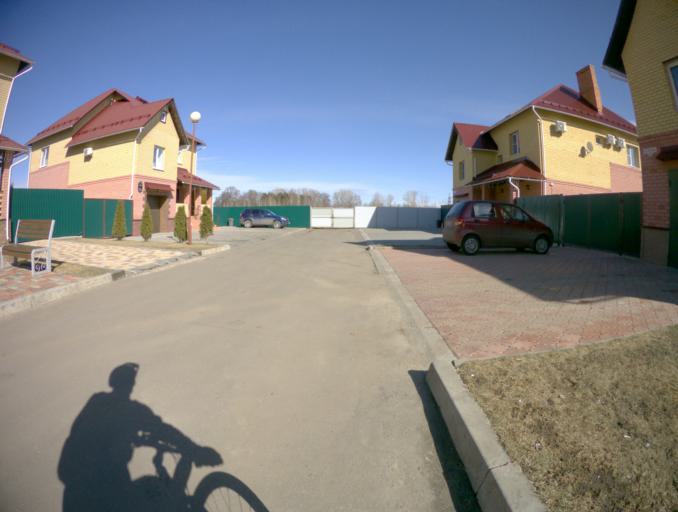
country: RU
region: Vladimir
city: Suzdal'
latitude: 56.4285
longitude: 40.4556
